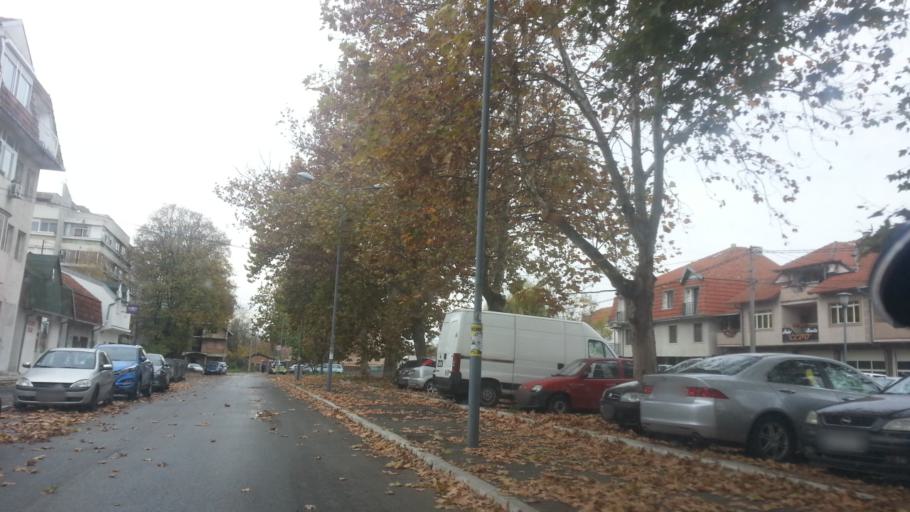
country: RS
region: Central Serbia
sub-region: Belgrade
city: Zemun
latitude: 44.8463
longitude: 20.3927
